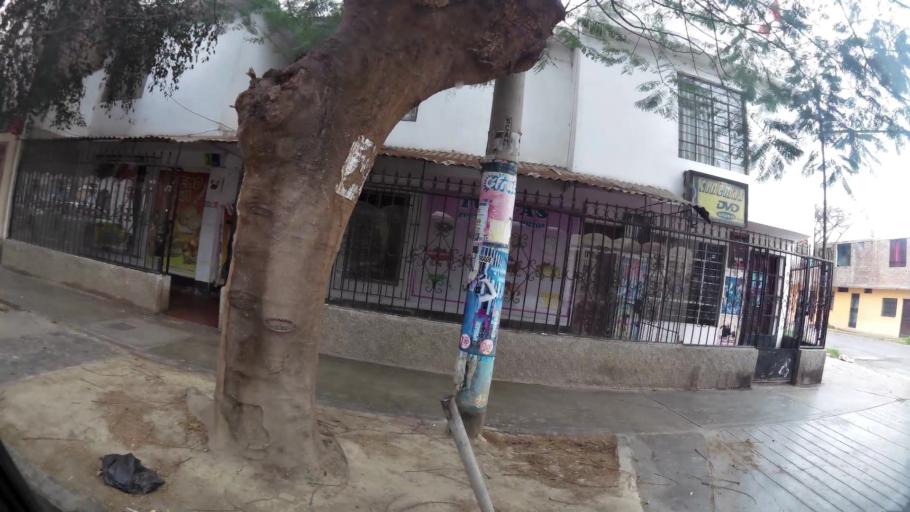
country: PE
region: La Libertad
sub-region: Provincia de Trujillo
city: Trujillo
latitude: -8.1210
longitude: -79.0309
